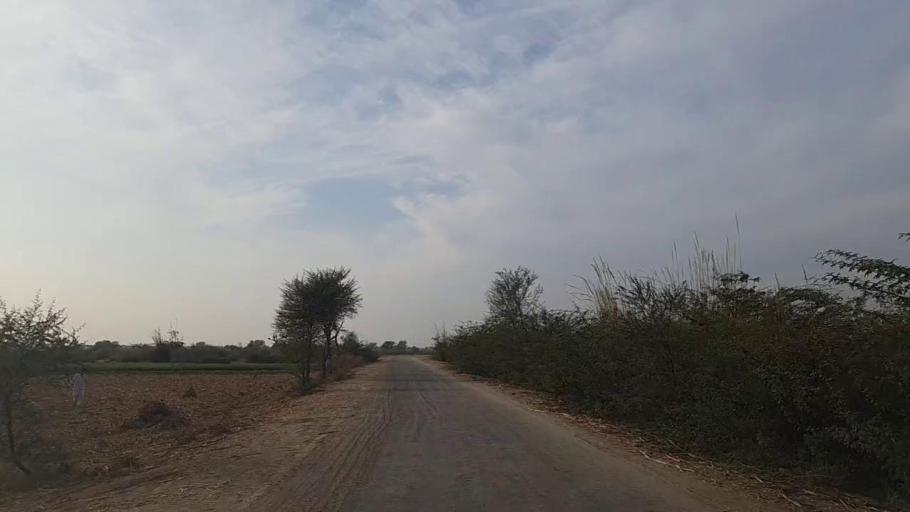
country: PK
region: Sindh
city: Daur
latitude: 26.5027
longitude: 68.4419
